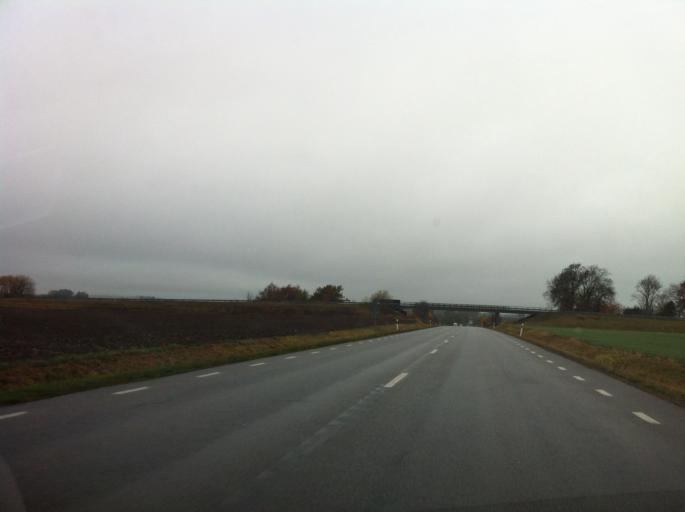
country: SE
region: Skane
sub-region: Kavlinge Kommun
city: Kaevlinge
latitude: 55.7820
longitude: 13.1337
